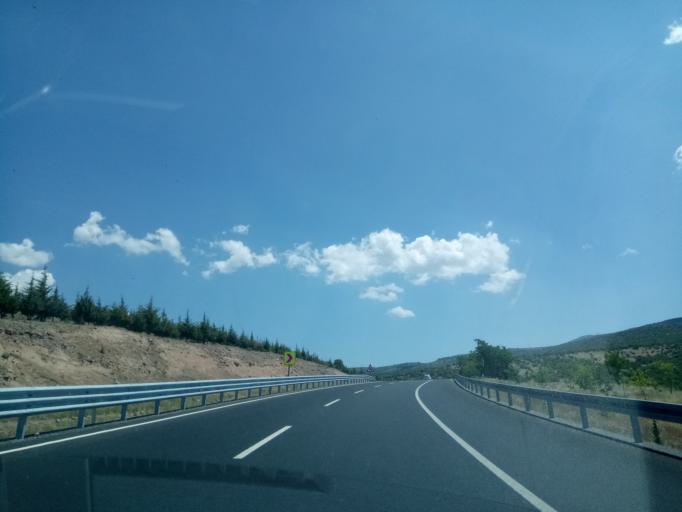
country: TR
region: Konya
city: Cavus
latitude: 37.6384
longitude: 31.9399
